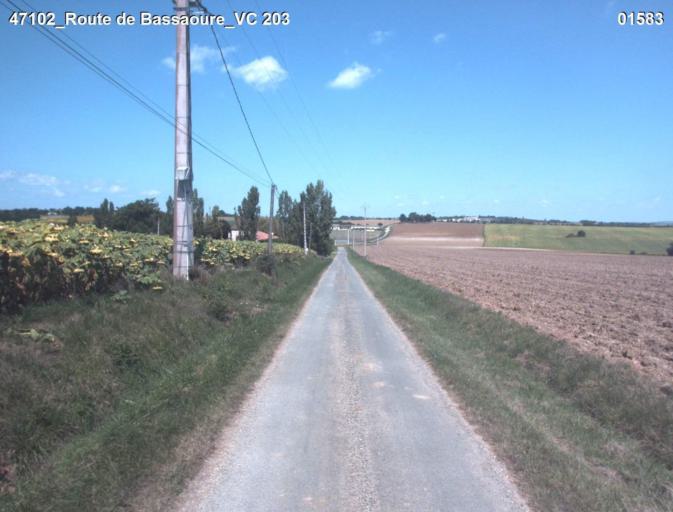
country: FR
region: Midi-Pyrenees
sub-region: Departement du Gers
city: Condom
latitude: 44.0479
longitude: 0.4301
